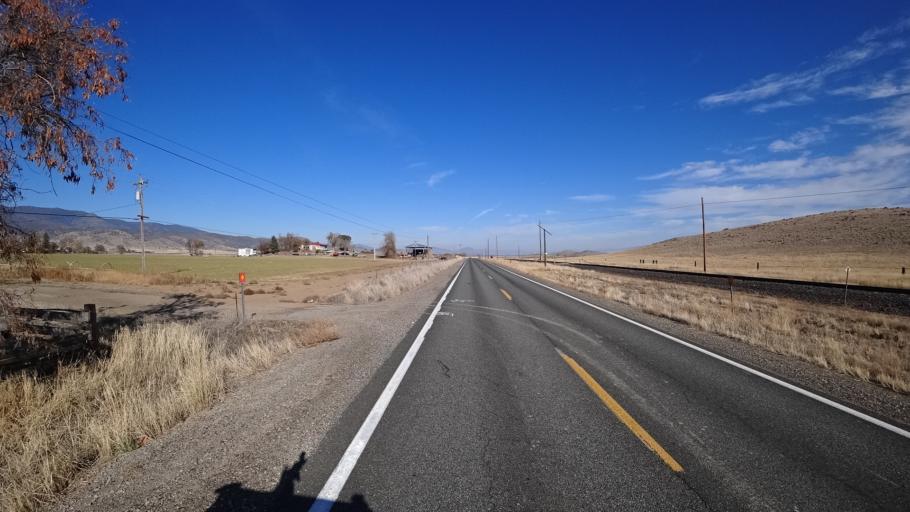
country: US
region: California
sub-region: Siskiyou County
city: Montague
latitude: 41.5529
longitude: -122.5262
